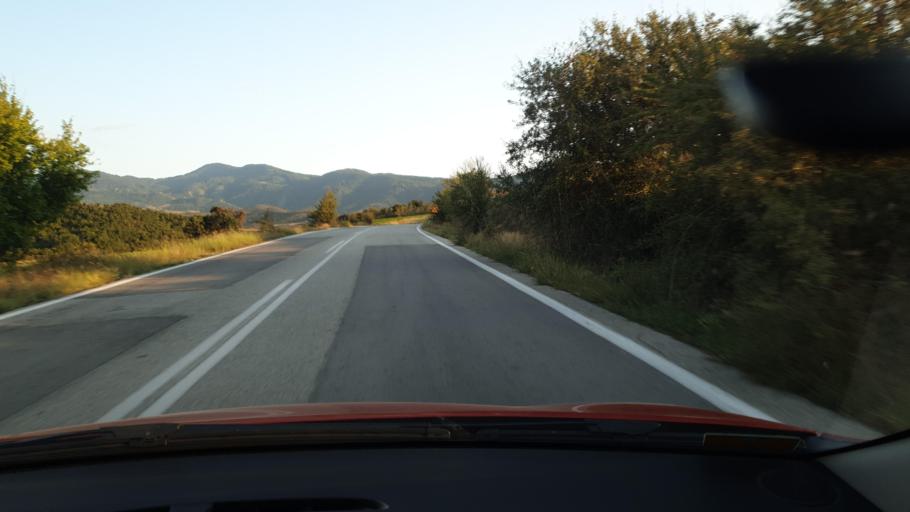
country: GR
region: Central Macedonia
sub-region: Nomos Thessalonikis
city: Nea Apollonia
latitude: 40.5202
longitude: 23.4725
